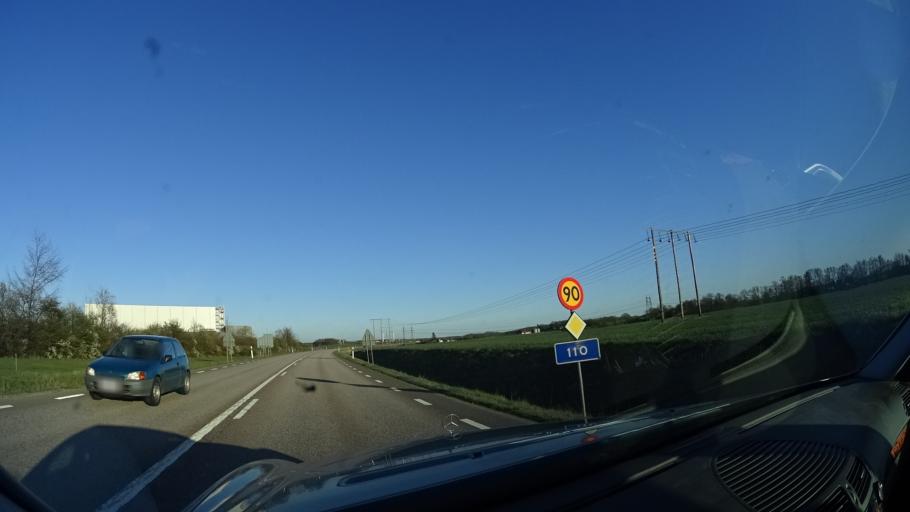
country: SE
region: Skane
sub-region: Bjuvs Kommun
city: Bjuv
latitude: 56.0714
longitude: 12.9349
